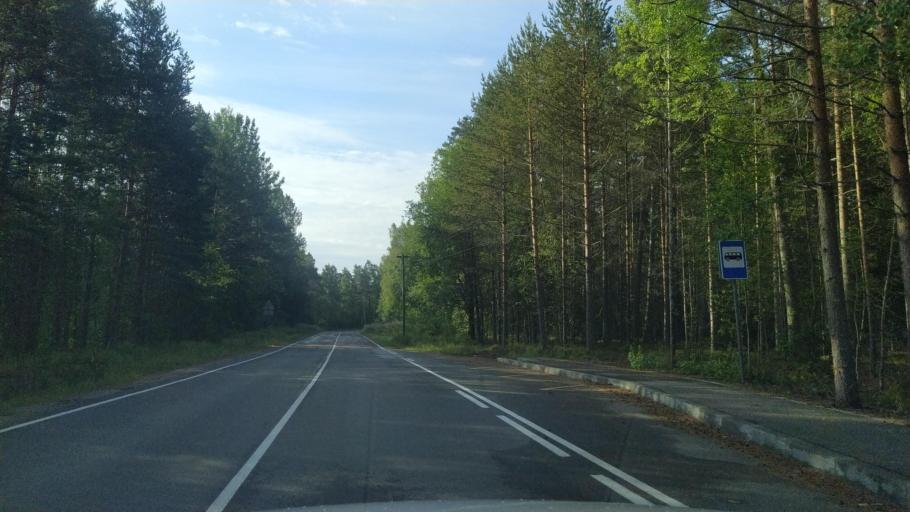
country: RU
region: Leningrad
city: Priozersk
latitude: 60.9758
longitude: 30.2790
